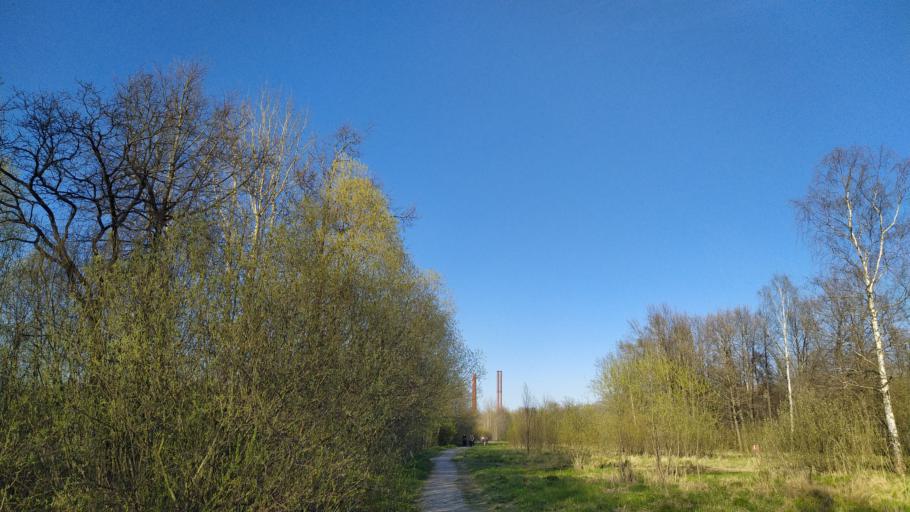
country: RU
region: St.-Petersburg
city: Pushkin
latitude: 59.7068
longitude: 30.3649
